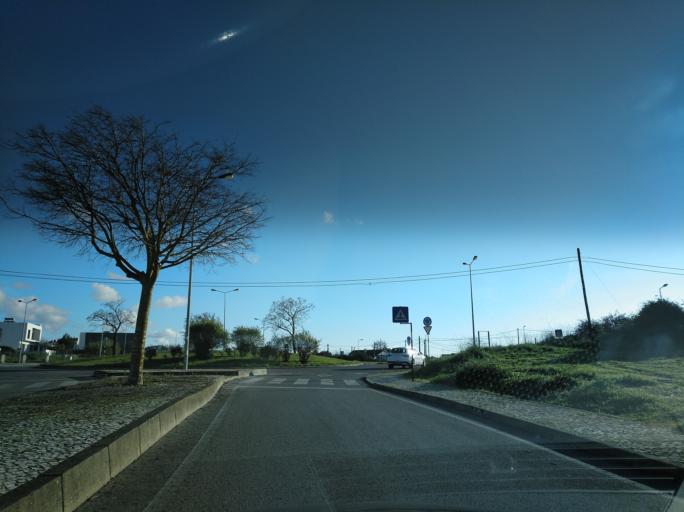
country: PT
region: Setubal
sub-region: Almada
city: Sobreda
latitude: 38.6560
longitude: -9.1886
